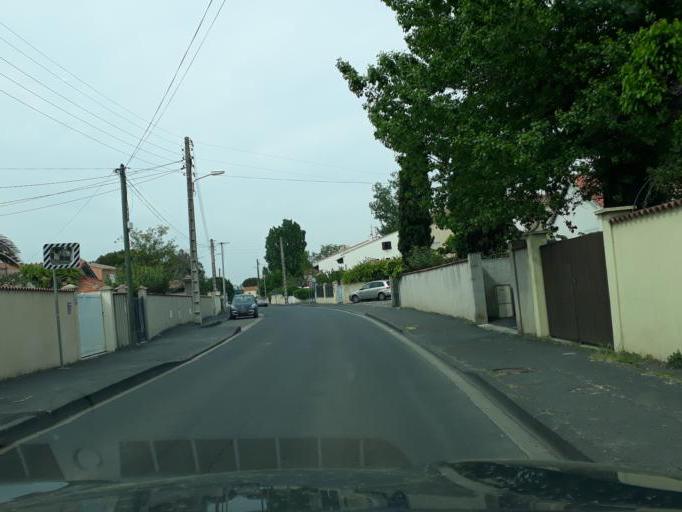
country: FR
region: Languedoc-Roussillon
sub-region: Departement de l'Herault
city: Agde
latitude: 43.2849
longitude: 3.4538
